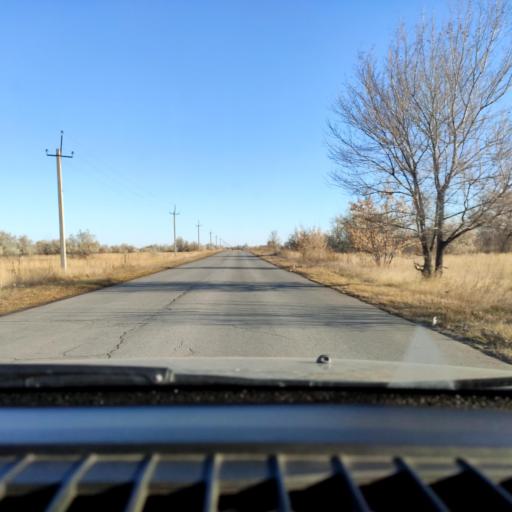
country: RU
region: Samara
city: Tol'yatti
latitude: 53.6515
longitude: 49.3240
